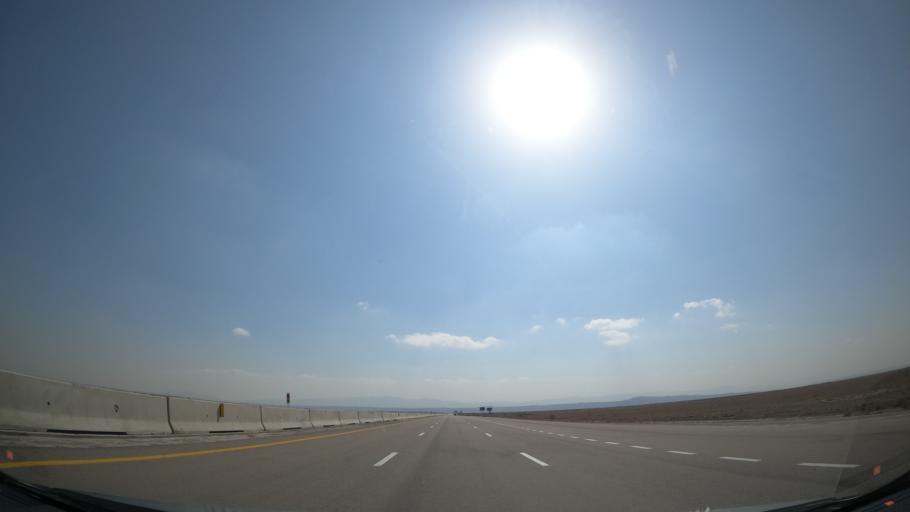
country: IR
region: Alborz
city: Nazarabad
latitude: 35.8698
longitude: 50.4788
